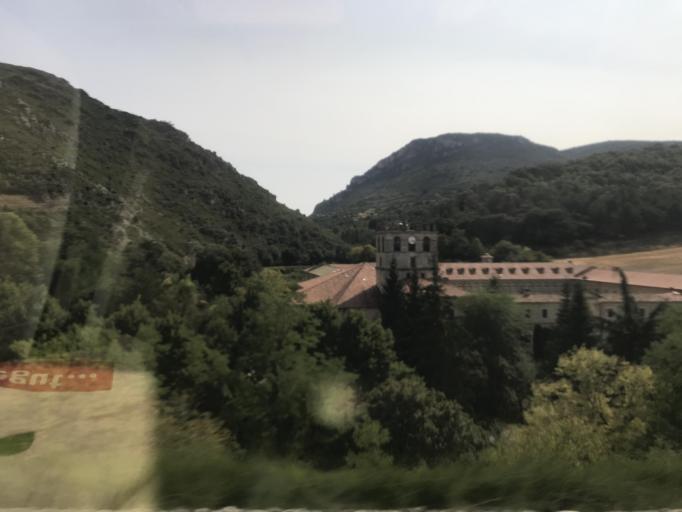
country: ES
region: Castille and Leon
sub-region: Provincia de Burgos
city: Bugedo
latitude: 42.6472
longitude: -3.0237
